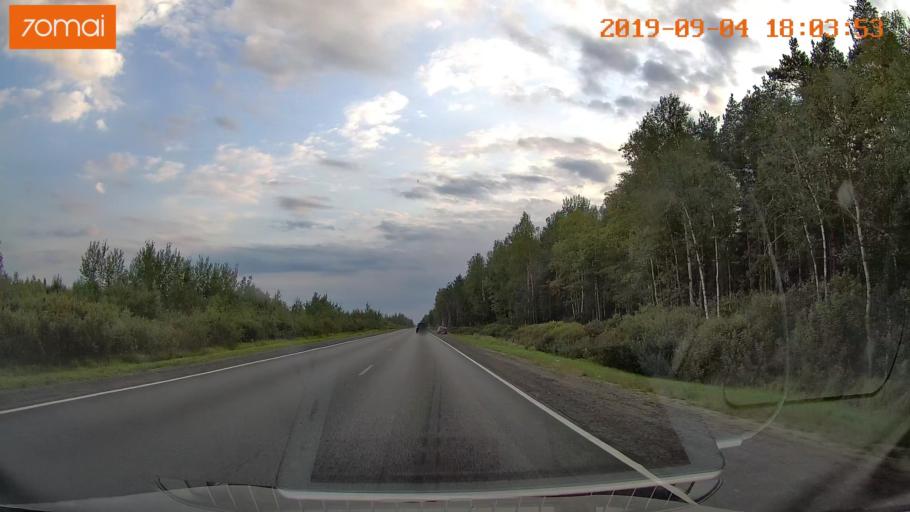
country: RU
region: Moskovskaya
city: Il'inskiy Pogost
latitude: 55.4586
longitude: 38.8465
